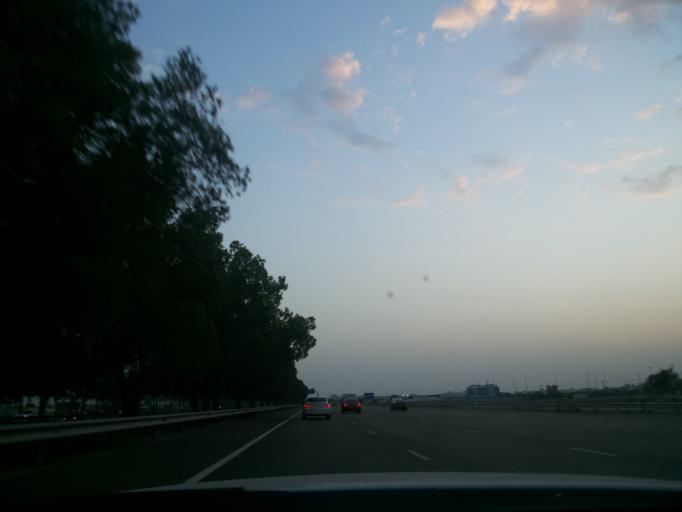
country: AE
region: Abu Dhabi
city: Abu Dhabi
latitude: 24.5823
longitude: 54.6995
